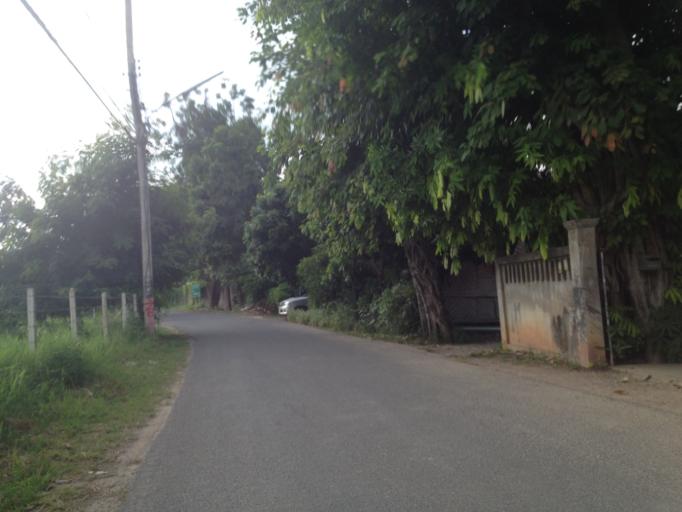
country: TH
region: Chiang Mai
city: Hang Dong
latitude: 18.7226
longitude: 98.9221
